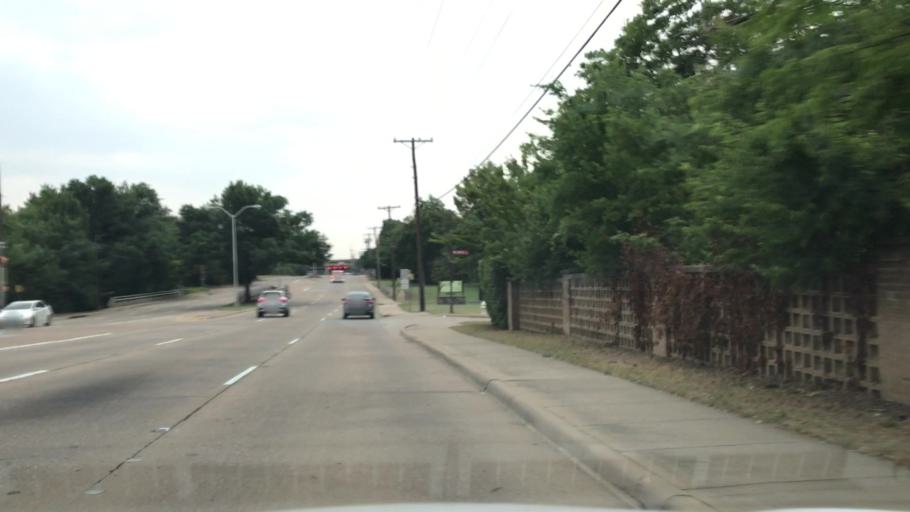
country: US
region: Texas
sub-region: Dallas County
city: Farmers Branch
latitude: 32.9166
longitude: -96.8818
